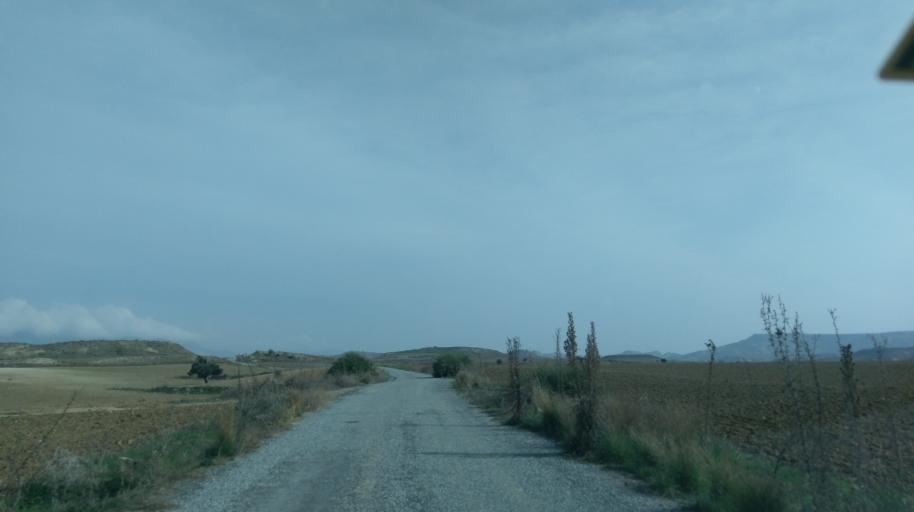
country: CY
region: Lefkosia
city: Morfou
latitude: 35.2493
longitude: 33.0691
